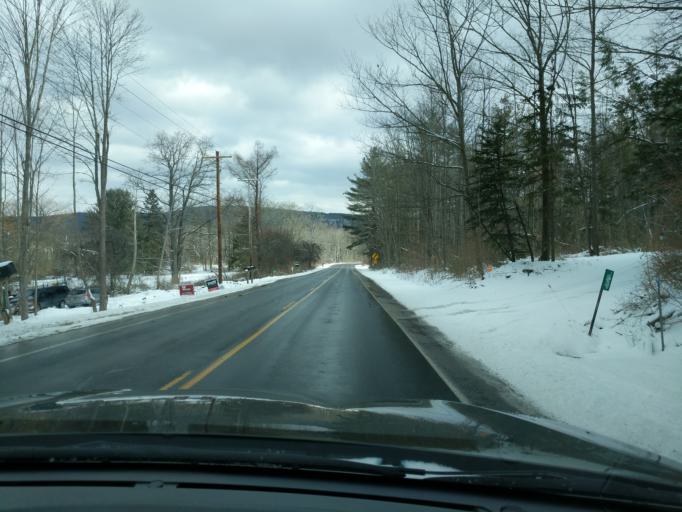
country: US
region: New York
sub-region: Tompkins County
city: Northeast Ithaca
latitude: 42.4277
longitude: -76.3982
